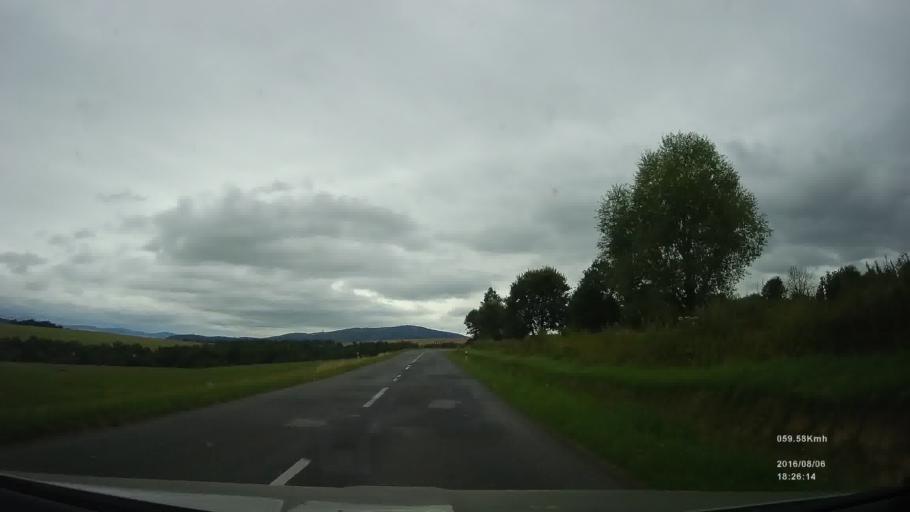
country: SK
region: Presovsky
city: Svidnik
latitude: 49.2869
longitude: 21.5717
